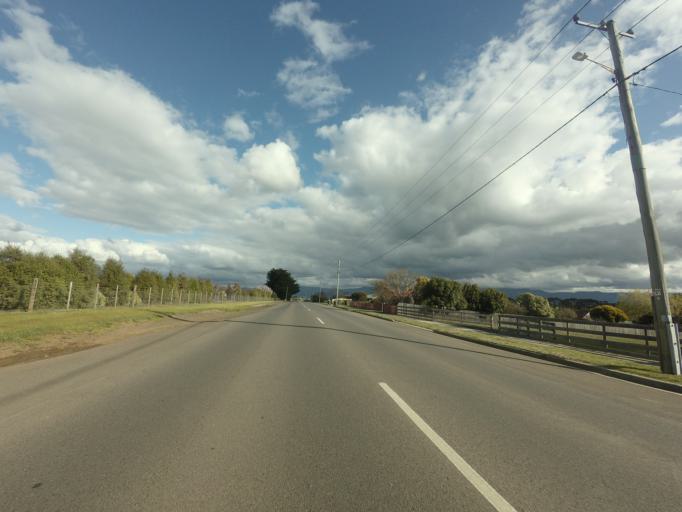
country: AU
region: Tasmania
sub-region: Northern Midlands
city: Longford
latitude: -41.6943
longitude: 147.0785
